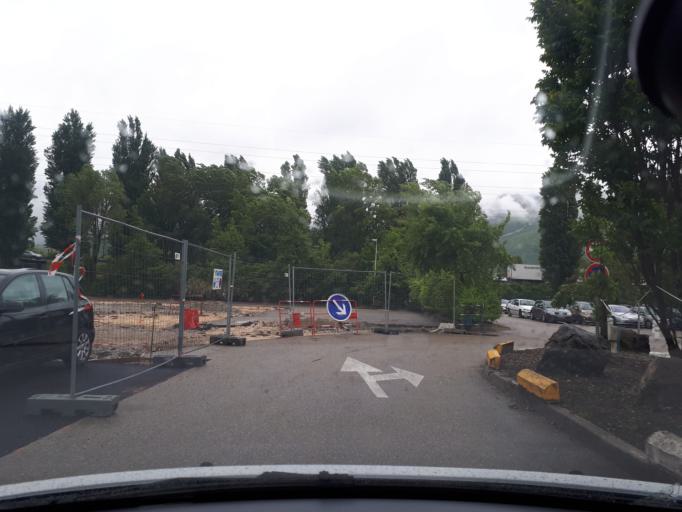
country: FR
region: Rhone-Alpes
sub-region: Departement de l'Isere
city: Fontaine
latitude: 45.2037
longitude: 5.6946
